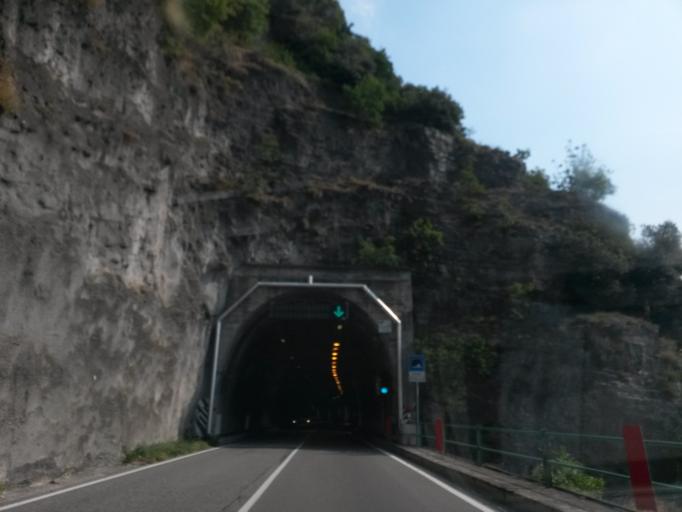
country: IT
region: Lombardy
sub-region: Provincia di Brescia
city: Gardola
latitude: 45.7186
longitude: 10.7068
